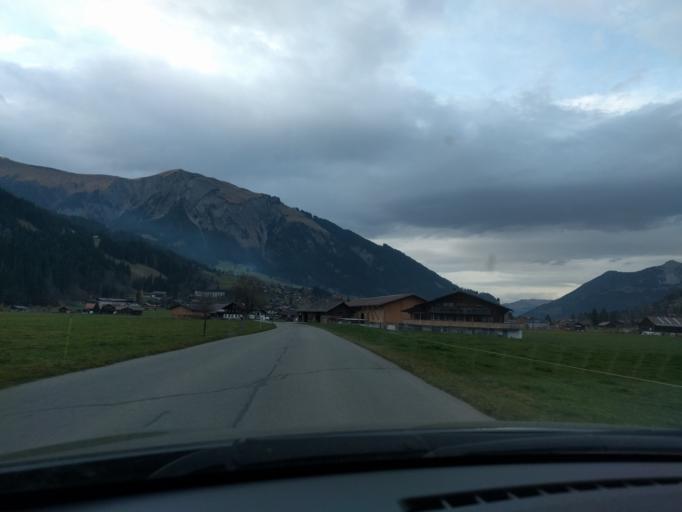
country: CH
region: Bern
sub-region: Obersimmental-Saanen District
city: Lenk
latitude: 46.4491
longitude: 7.4497
